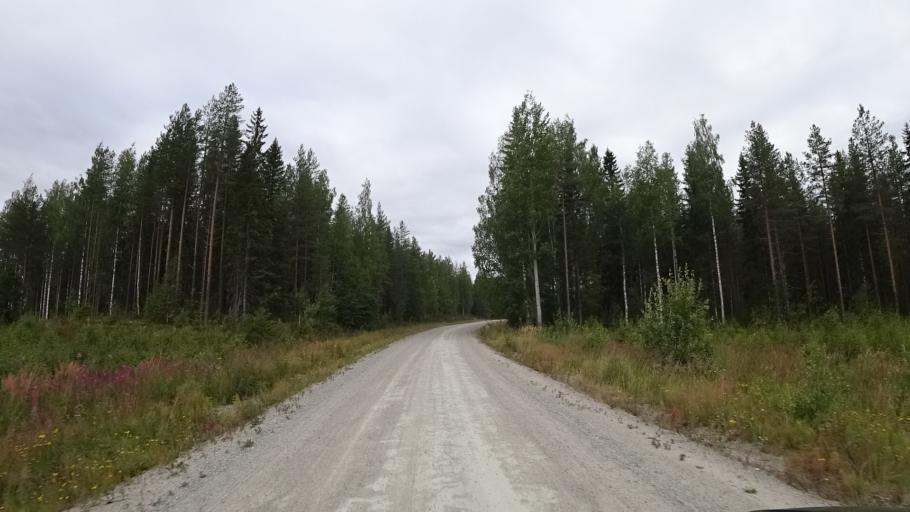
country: FI
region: North Karelia
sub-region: Joensuu
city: Ilomantsi
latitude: 63.1541
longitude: 30.6152
